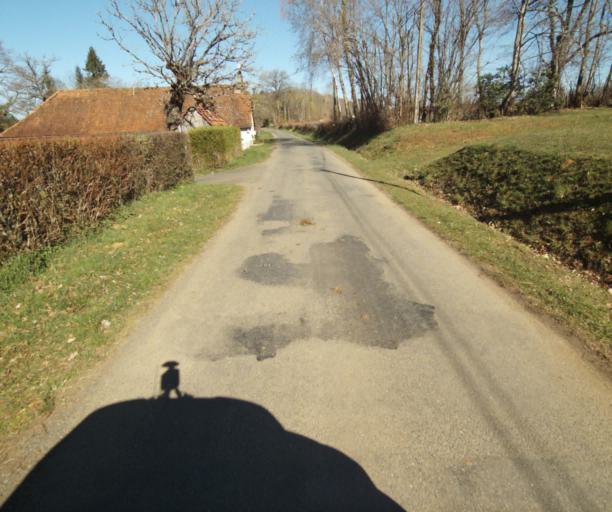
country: FR
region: Limousin
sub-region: Departement de la Correze
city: Seilhac
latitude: 45.3895
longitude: 1.7545
